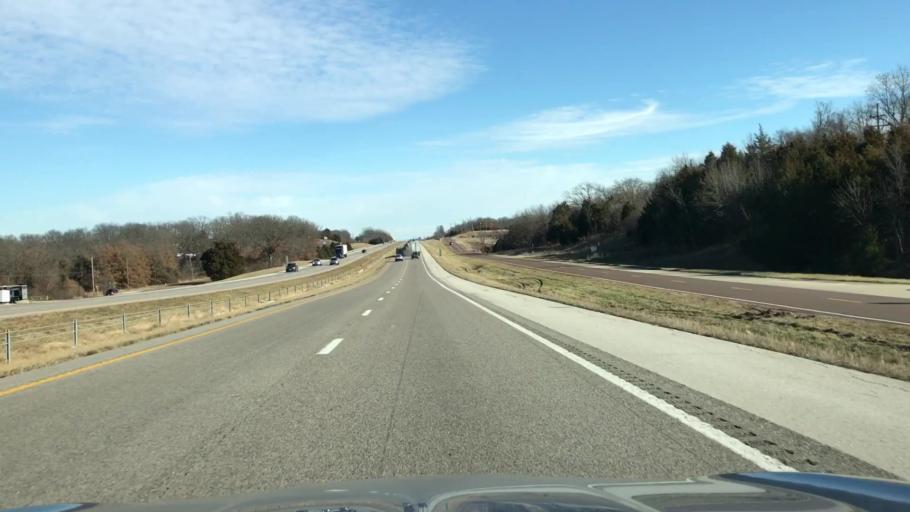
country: US
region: Missouri
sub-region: Warren County
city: Warrenton
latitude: 38.8188
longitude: -91.1086
